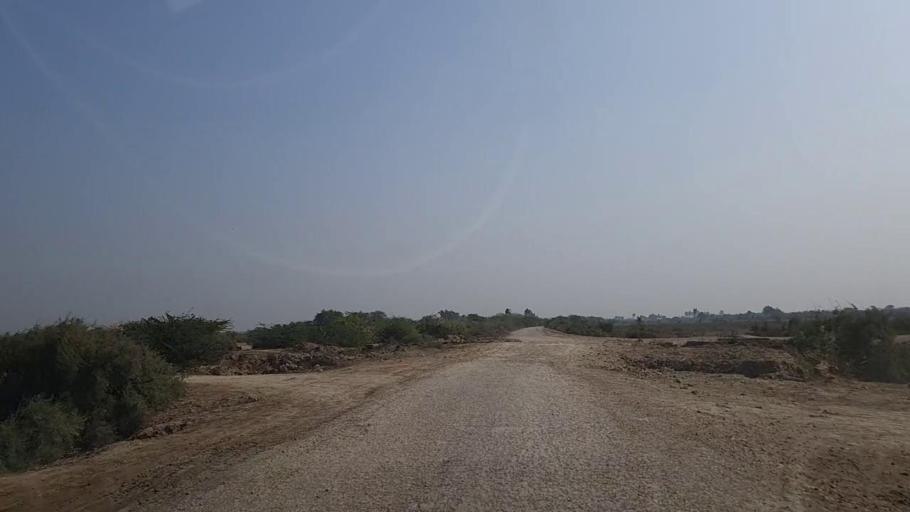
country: PK
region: Sindh
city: Keti Bandar
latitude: 24.2517
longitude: 67.6282
